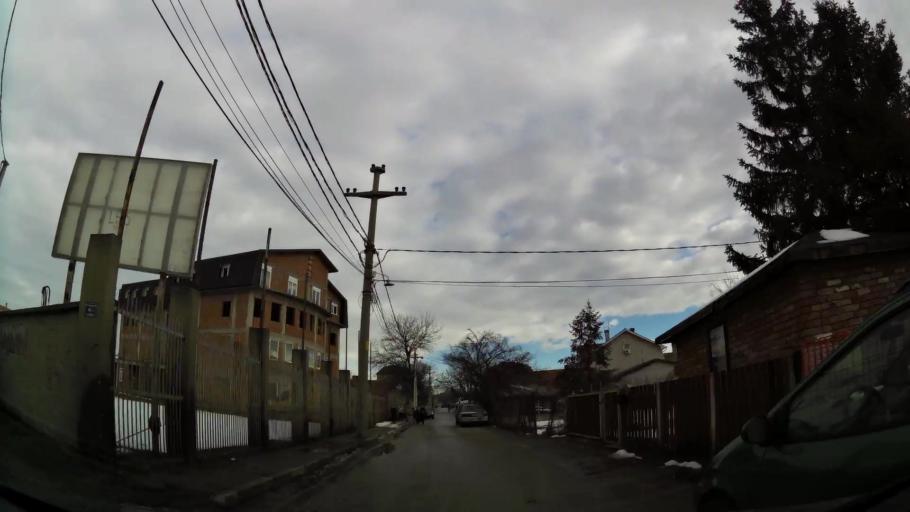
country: RS
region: Central Serbia
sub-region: Belgrade
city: Zemun
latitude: 44.8054
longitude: 20.3568
